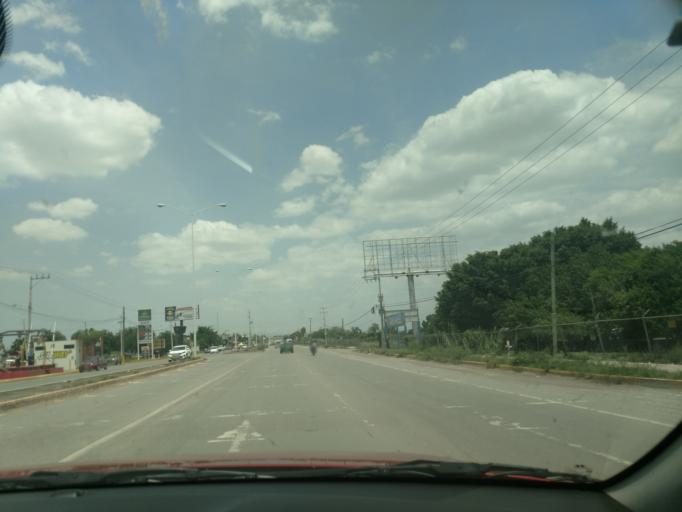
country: MX
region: San Luis Potosi
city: Ciudad Fernandez
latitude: 21.9358
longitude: -100.0271
